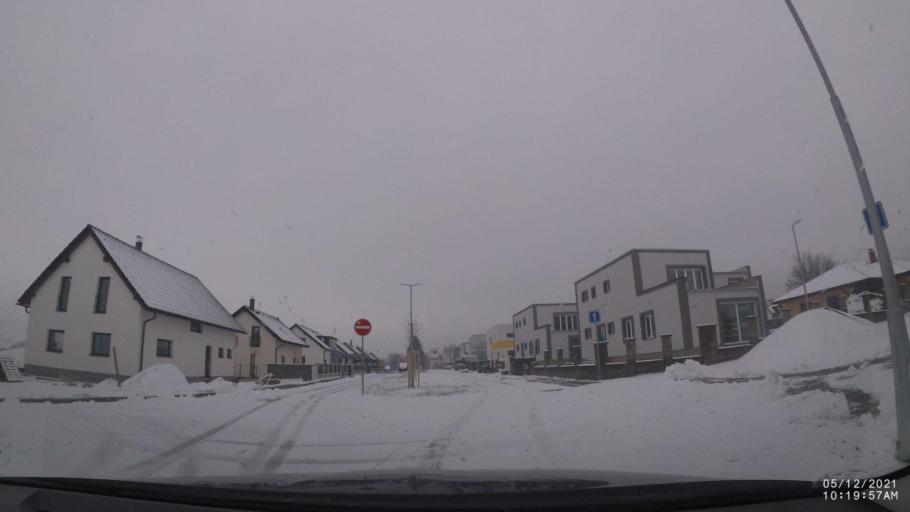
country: CZ
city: Vamberk
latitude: 50.1119
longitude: 16.2879
